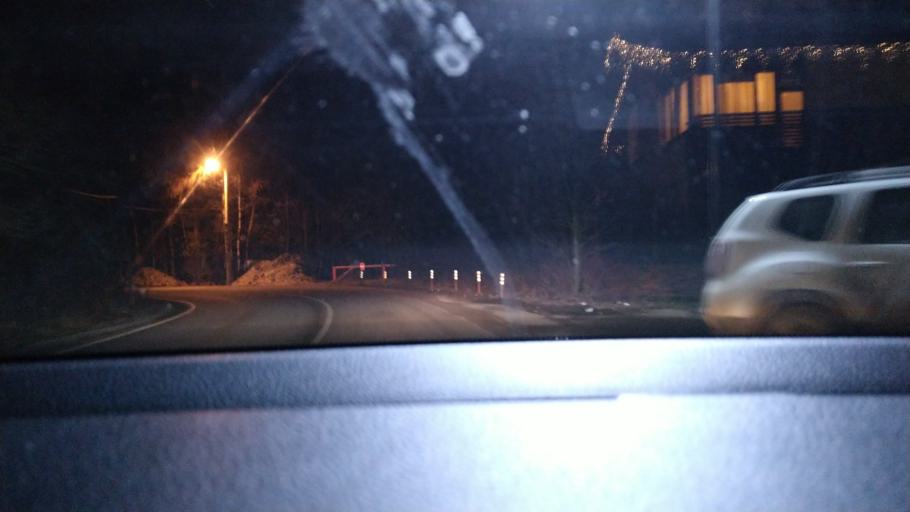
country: RU
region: Moskovskaya
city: Opalikha
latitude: 55.8010
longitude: 37.2694
